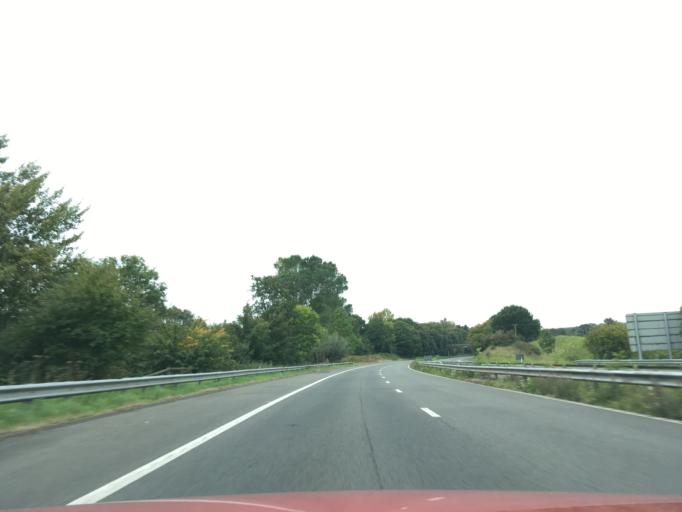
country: GB
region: Wales
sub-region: Monmouthshire
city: Chepstow
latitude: 51.6169
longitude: -2.6967
